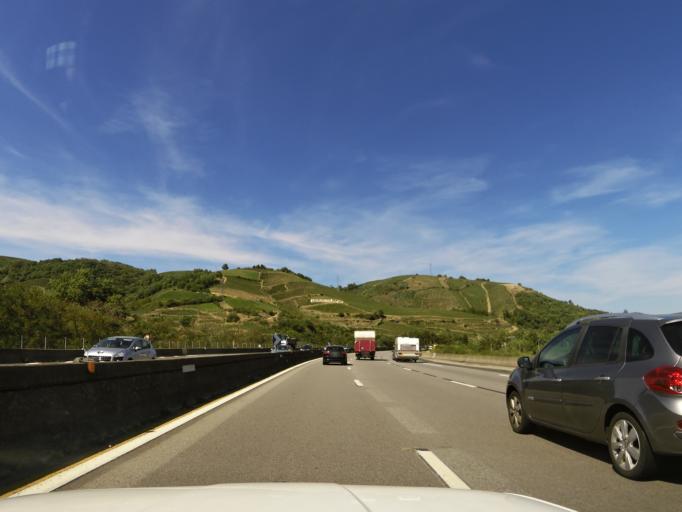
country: FR
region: Rhone-Alpes
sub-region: Departement du Rhone
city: Saint-Cyr-sur-le-Rhone
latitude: 45.5024
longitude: 4.8390
